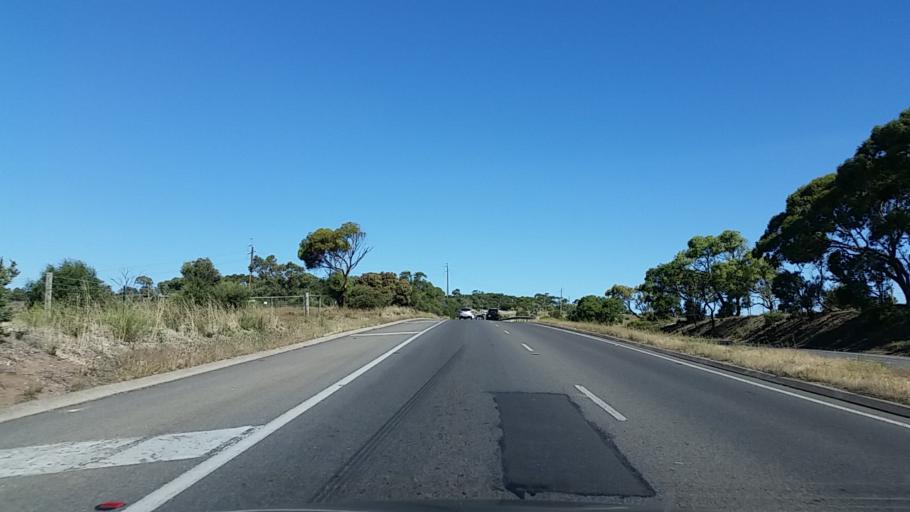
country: AU
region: South Australia
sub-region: Adelaide Hills
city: Seacliff
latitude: -35.0479
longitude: 138.5325
